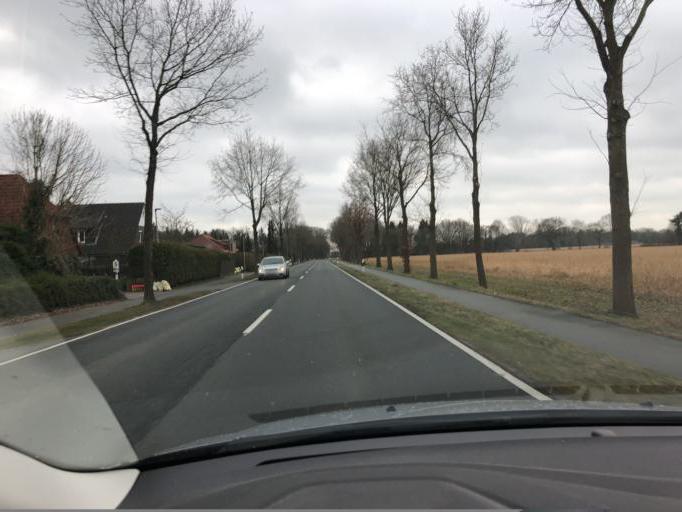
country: DE
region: Lower Saxony
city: Wiefelstede
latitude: 53.1768
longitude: 8.1294
